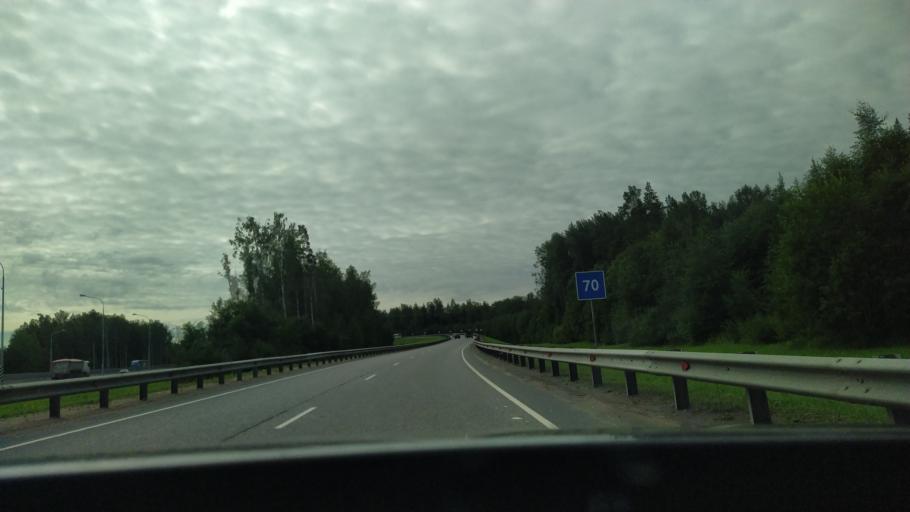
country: RU
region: Leningrad
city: Ul'yanovka
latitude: 59.5974
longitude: 30.7728
